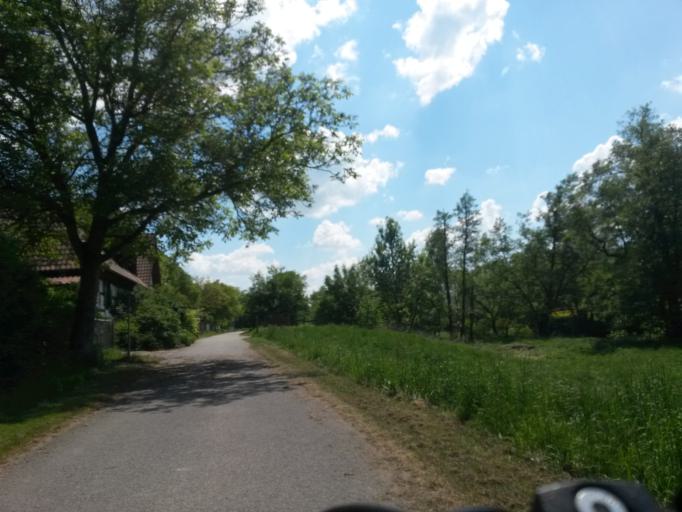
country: DE
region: Bavaria
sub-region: Regierungsbezirk Unterfranken
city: Bad Kissingen
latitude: 50.2234
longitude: 10.0663
